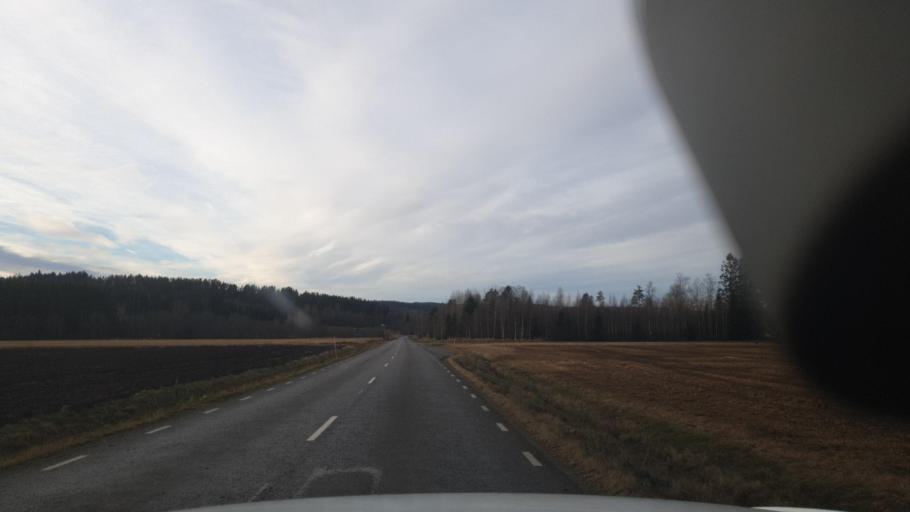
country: SE
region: Vaermland
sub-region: Eda Kommun
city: Amotfors
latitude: 59.6813
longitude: 12.1417
